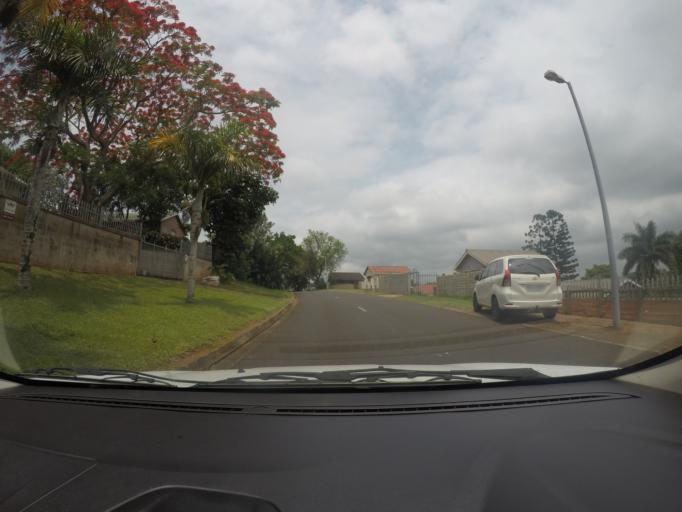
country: ZA
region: KwaZulu-Natal
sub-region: uThungulu District Municipality
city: Empangeni
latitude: -28.7526
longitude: 31.8900
